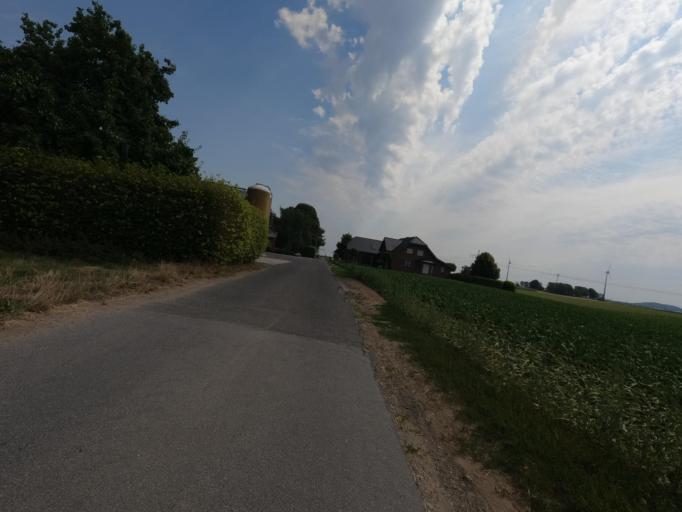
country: DE
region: North Rhine-Westphalia
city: Baesweiler
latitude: 50.9146
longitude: 6.2081
